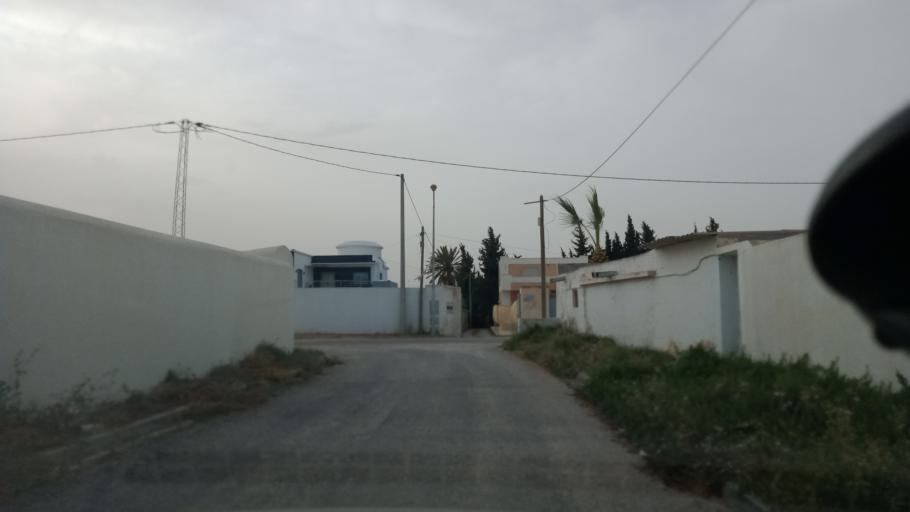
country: TN
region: Safaqis
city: Al Qarmadah
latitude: 34.7881
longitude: 10.7639
